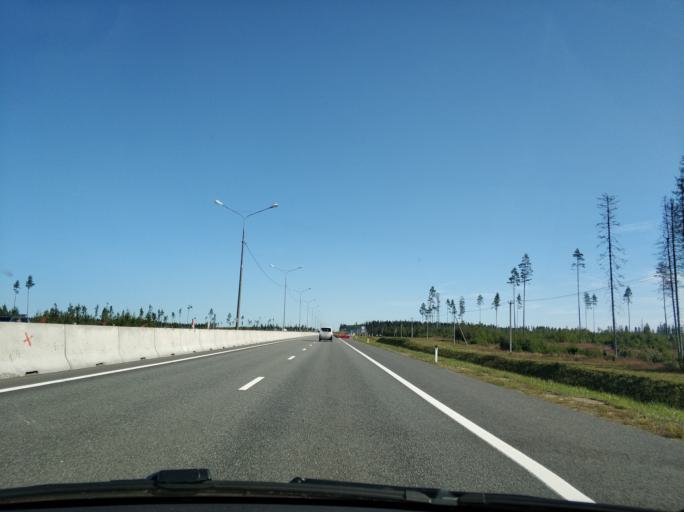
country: RU
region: Leningrad
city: Sosnovo
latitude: 60.4720
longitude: 30.1960
